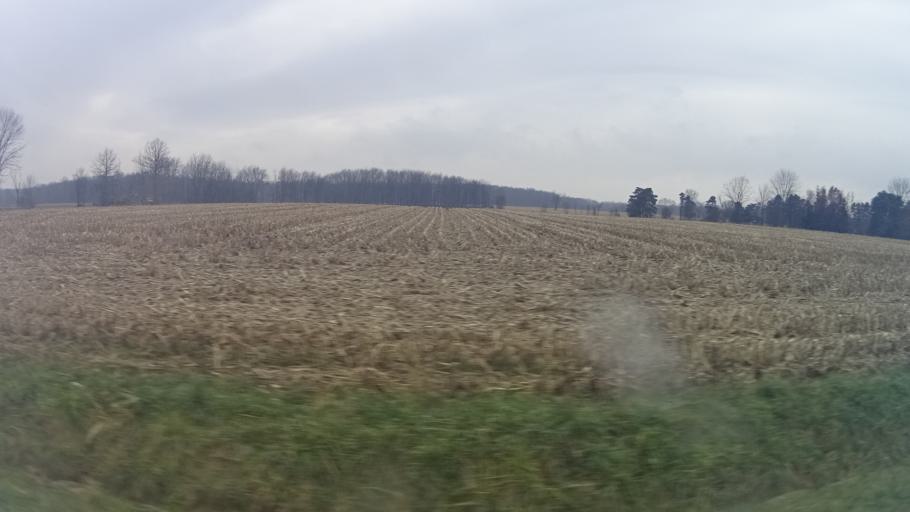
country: US
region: Ohio
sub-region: Lorain County
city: Lagrange
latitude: 41.2193
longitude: -82.1579
